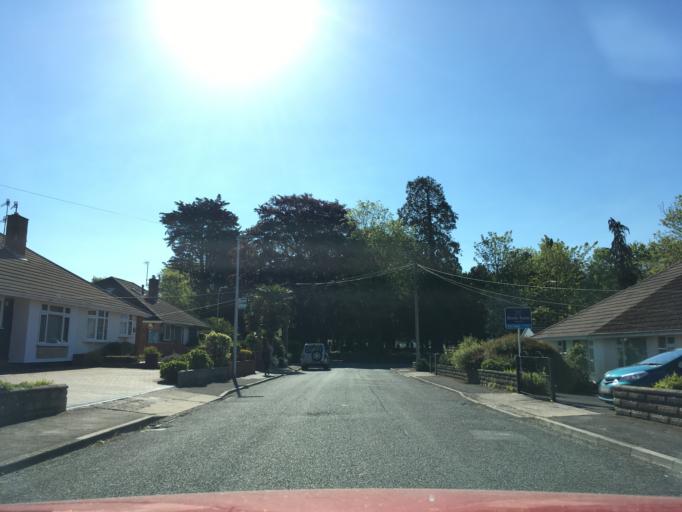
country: GB
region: England
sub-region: North Somerset
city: Portishead
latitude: 51.4734
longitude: -2.7747
